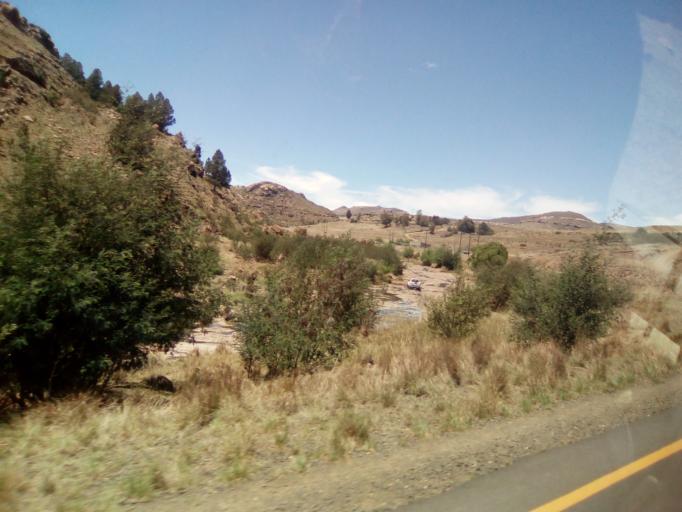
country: LS
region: Qacha's Nek
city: Qacha's Nek
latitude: -30.1029
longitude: 28.6564
